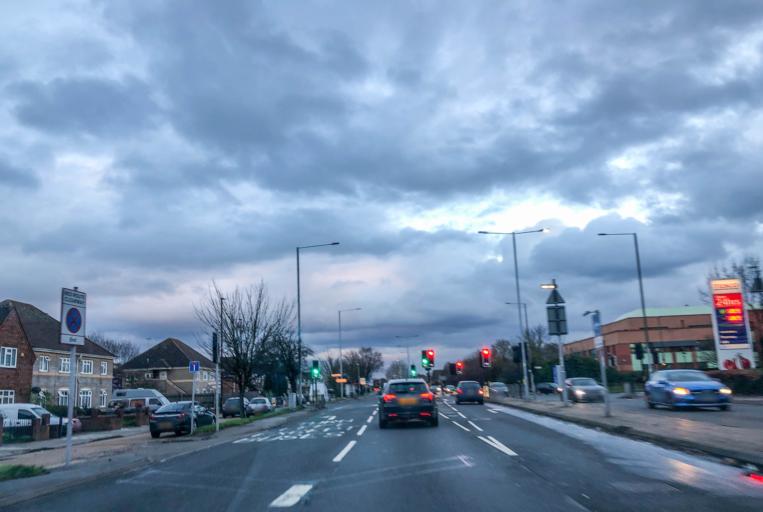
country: GB
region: England
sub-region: Greater London
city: Feltham
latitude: 51.4600
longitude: -0.4128
